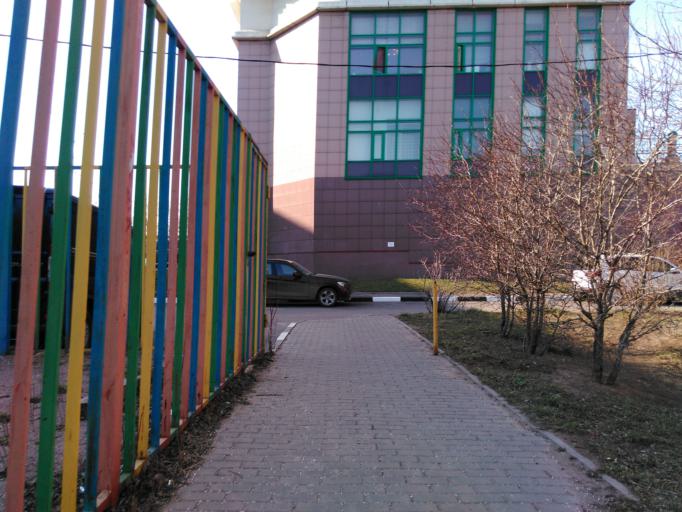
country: RU
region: Moscow
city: Ramenki
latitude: 55.6776
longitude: 37.5109
